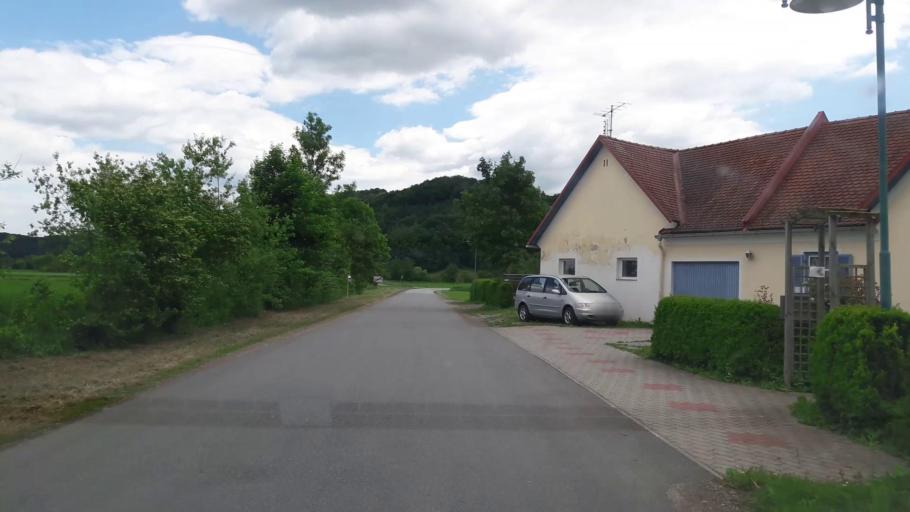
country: AT
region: Styria
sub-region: Politischer Bezirk Hartberg-Fuerstenfeld
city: UEbersbach
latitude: 47.0136
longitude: 16.0478
